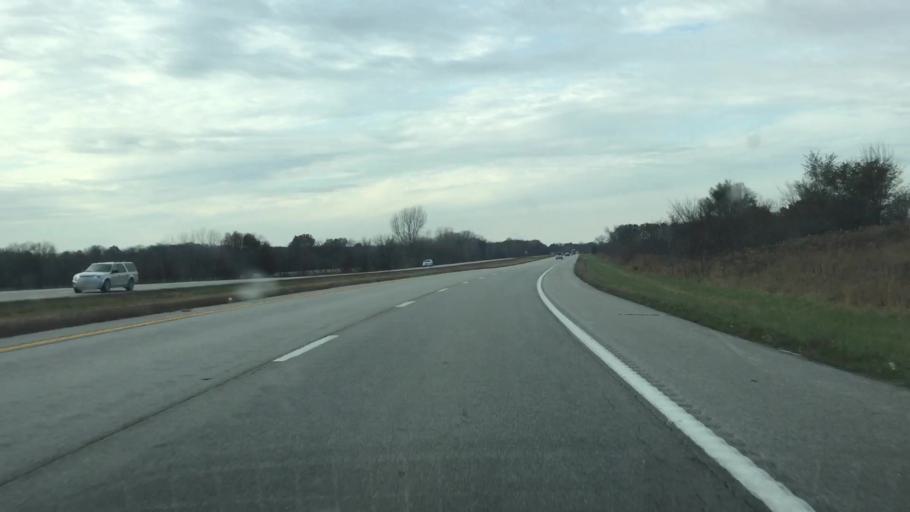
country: US
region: Missouri
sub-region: Cass County
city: Garden City
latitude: 38.5074
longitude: -94.0950
